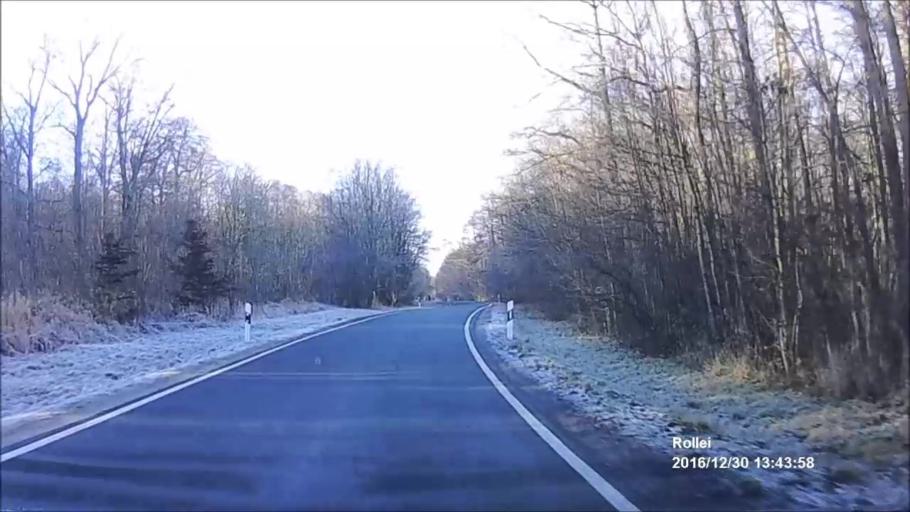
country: DE
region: Thuringia
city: Rockhausen
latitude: 50.9177
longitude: 11.0877
